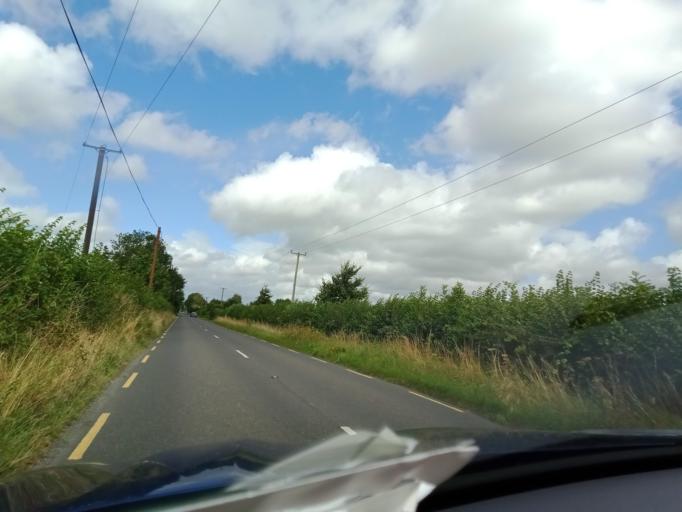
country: IE
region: Leinster
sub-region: Laois
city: Portlaoise
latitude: 52.9916
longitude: -7.2833
